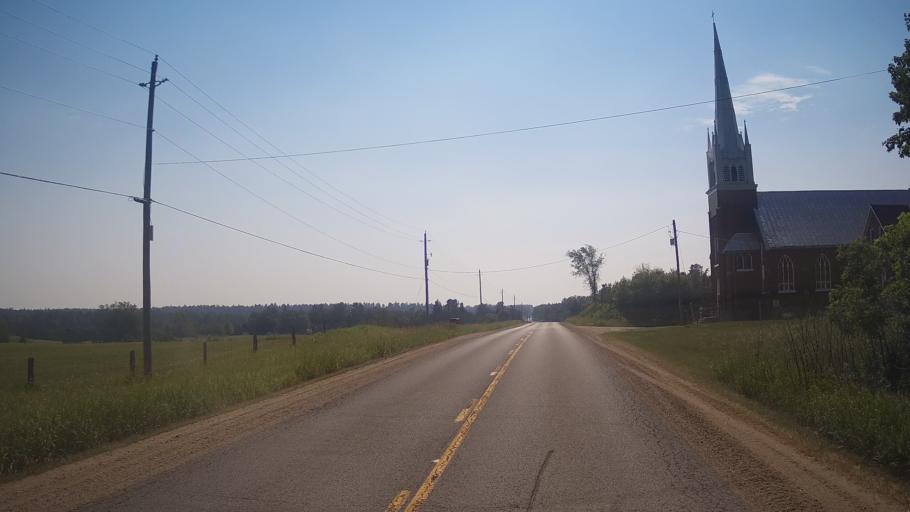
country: CA
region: Ontario
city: Pembroke
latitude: 45.6132
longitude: -77.1929
